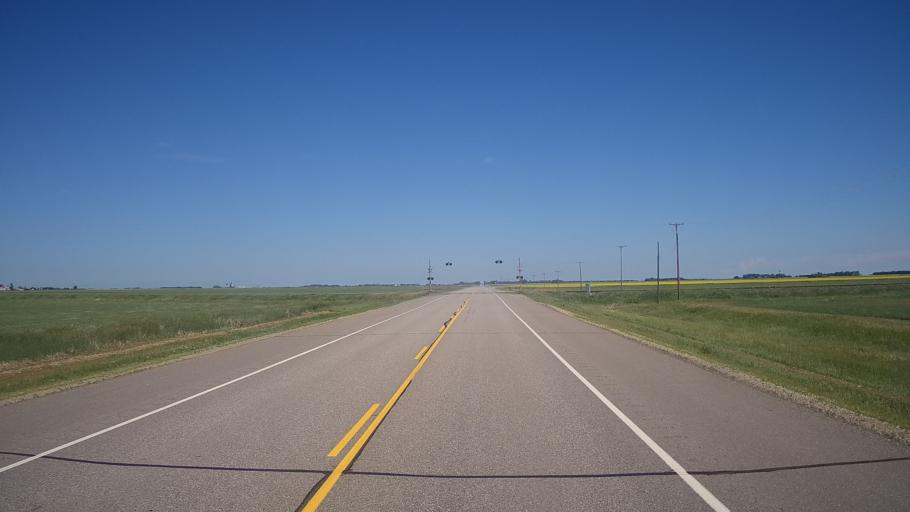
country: CA
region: Manitoba
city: Portage la Prairie
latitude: 50.0078
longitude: -98.4688
